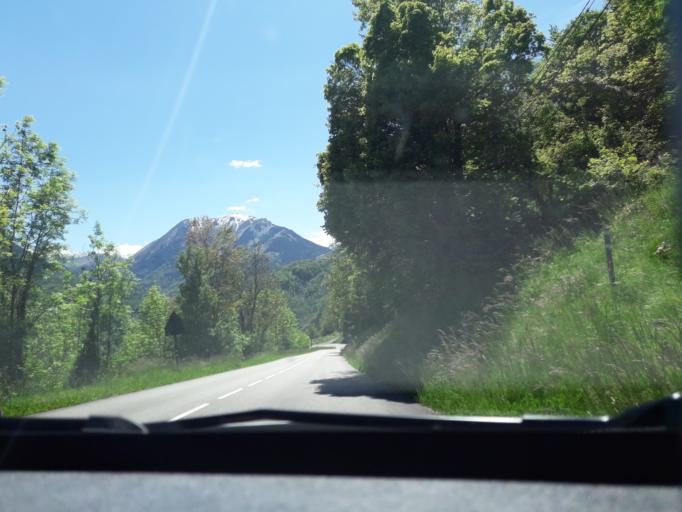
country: FR
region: Rhone-Alpes
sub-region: Departement de la Savoie
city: Salins-les-Thermes
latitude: 45.4535
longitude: 6.5060
